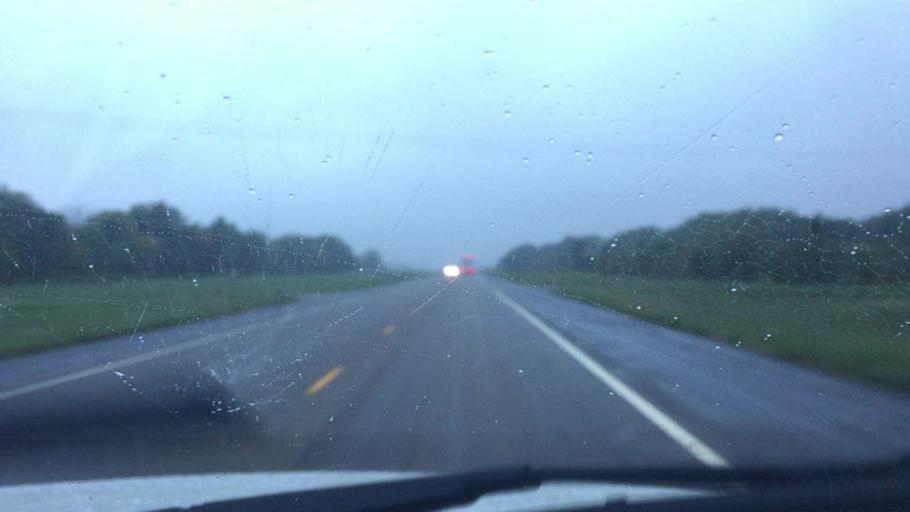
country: US
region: Kansas
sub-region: Montgomery County
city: Cherryvale
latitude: 37.4133
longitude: -95.4981
